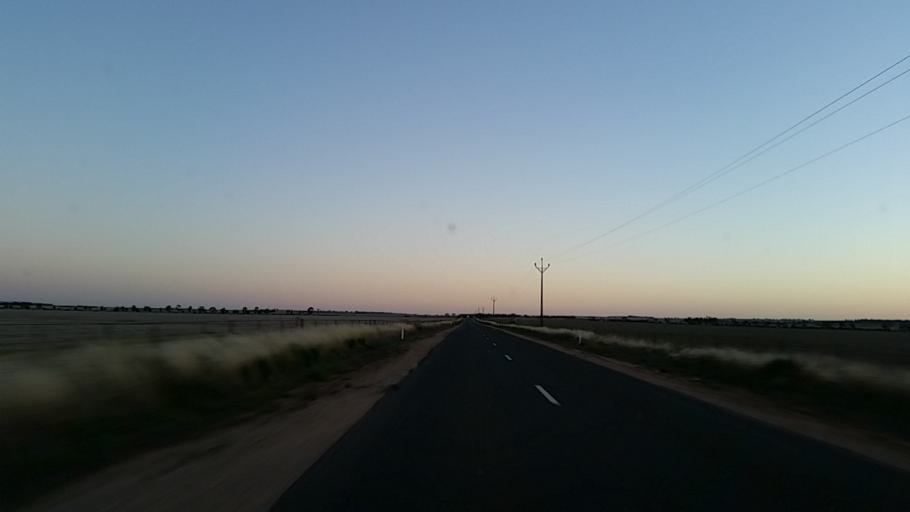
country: AU
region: South Australia
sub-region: Clare and Gilbert Valleys
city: Clare
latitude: -33.9303
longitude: 138.4913
